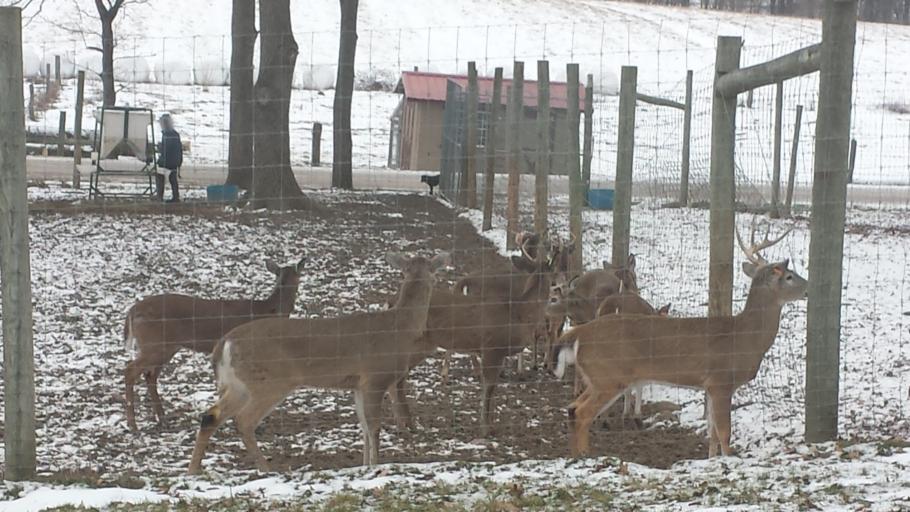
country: US
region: Ohio
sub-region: Holmes County
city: Millersburg
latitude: 40.5945
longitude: -81.8018
